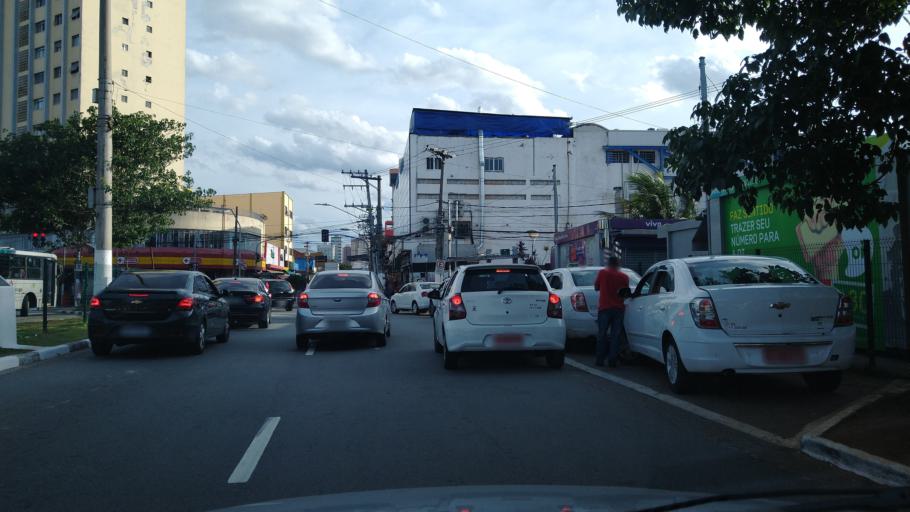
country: BR
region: Sao Paulo
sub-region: Osasco
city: Osasco
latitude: -23.5284
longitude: -46.7757
